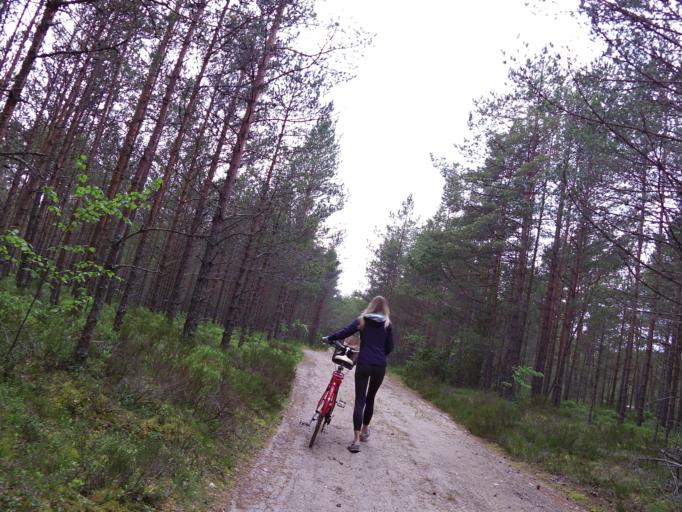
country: EE
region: Harju
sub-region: Paldiski linn
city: Paldiski
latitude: 59.2426
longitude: 23.7462
